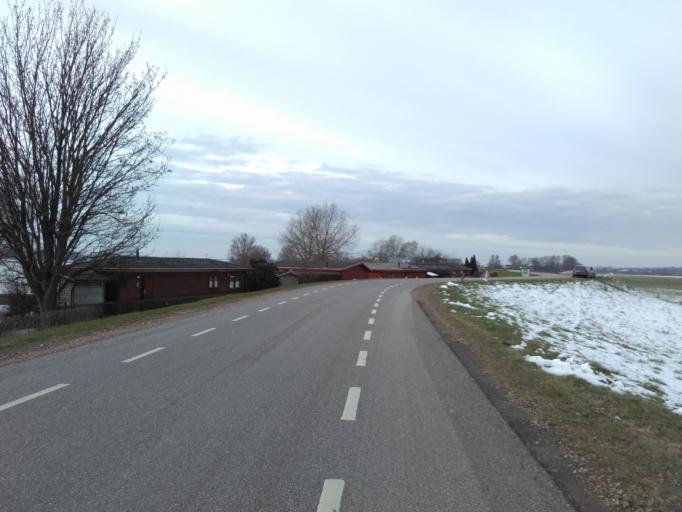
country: NL
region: Gelderland
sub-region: Gemeente Overbetuwe
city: Oosterhout
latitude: 51.8761
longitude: 5.8069
